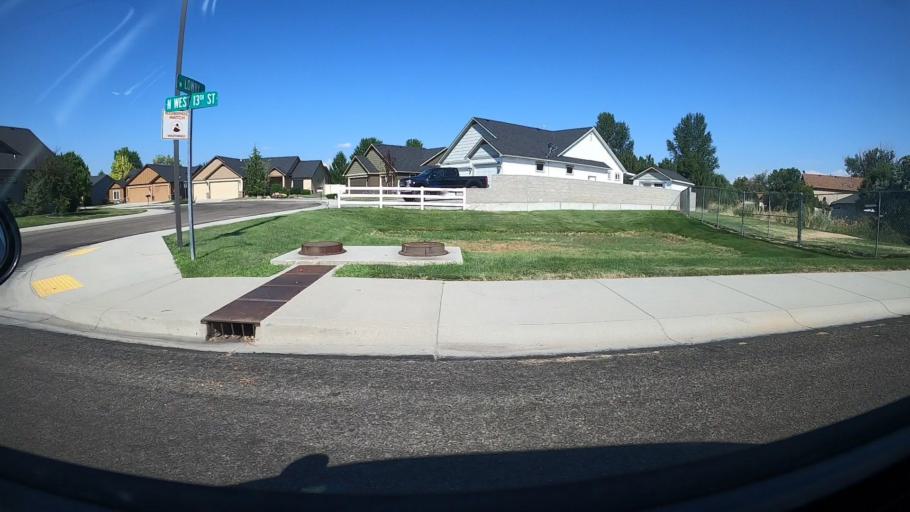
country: US
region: Idaho
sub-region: Ada County
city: Meridian
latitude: 43.6304
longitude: -116.4098
